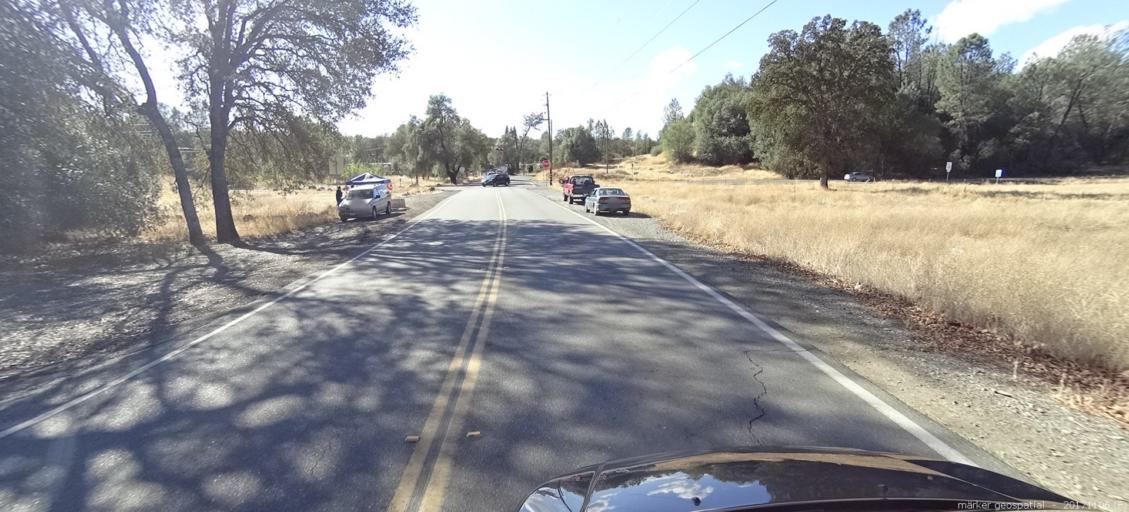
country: US
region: California
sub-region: Shasta County
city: Palo Cedro
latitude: 40.5889
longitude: -122.3058
